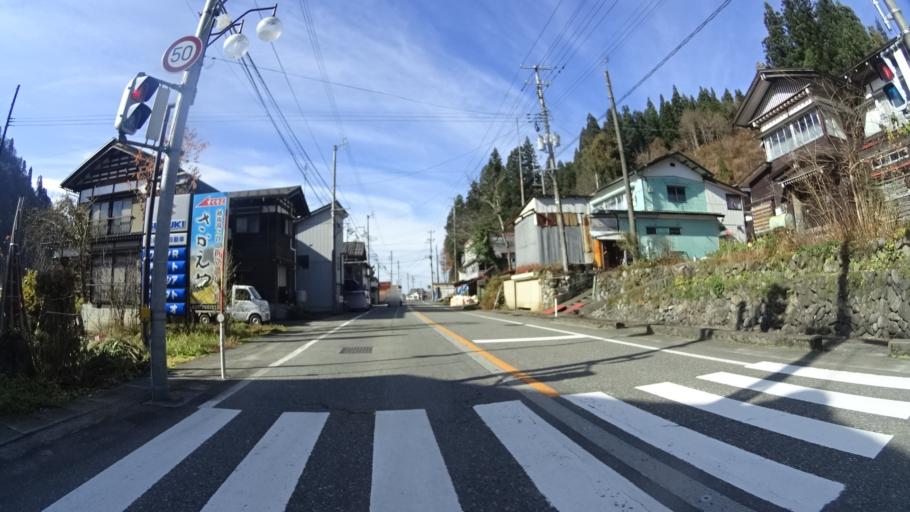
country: JP
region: Niigata
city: Muikamachi
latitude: 37.2080
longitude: 139.0625
